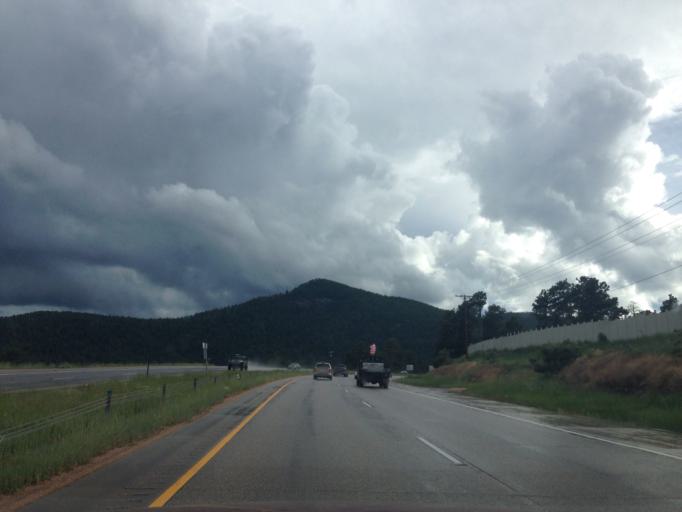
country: US
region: Colorado
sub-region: Jefferson County
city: Indian Hills
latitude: 39.5493
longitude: -105.2553
